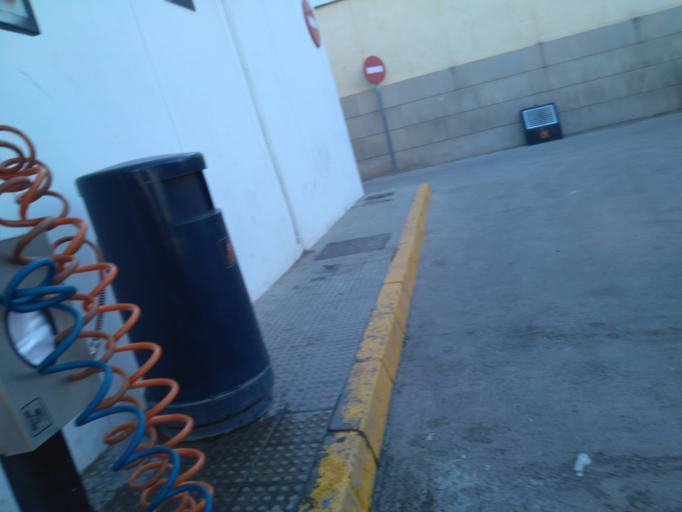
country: ES
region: Valencia
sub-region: Provincia de Valencia
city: Tavernes Blanques
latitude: 39.4931
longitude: -0.3869
